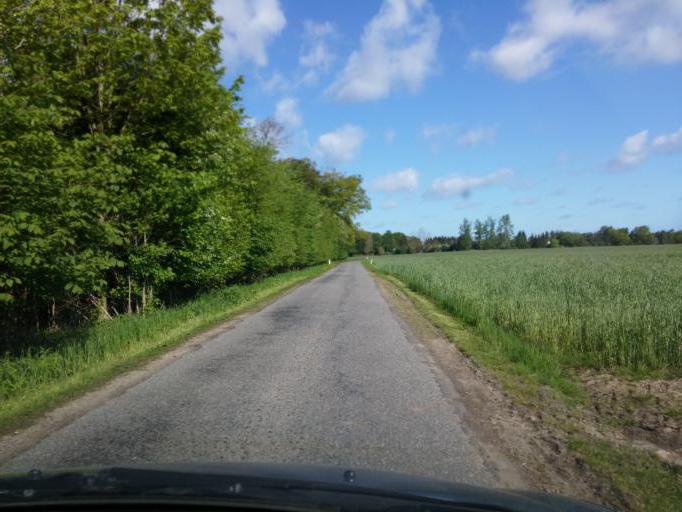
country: DK
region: South Denmark
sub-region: Kerteminde Kommune
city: Munkebo
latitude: 55.4147
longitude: 10.5359
